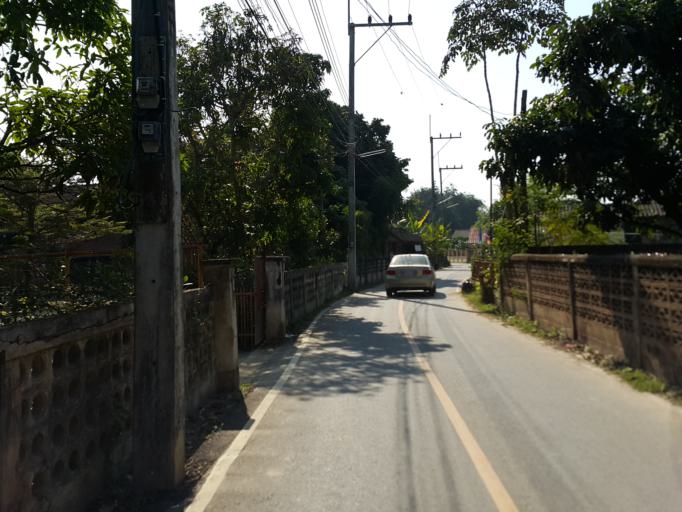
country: TH
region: Chiang Mai
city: San Sai
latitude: 18.8028
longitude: 99.0740
